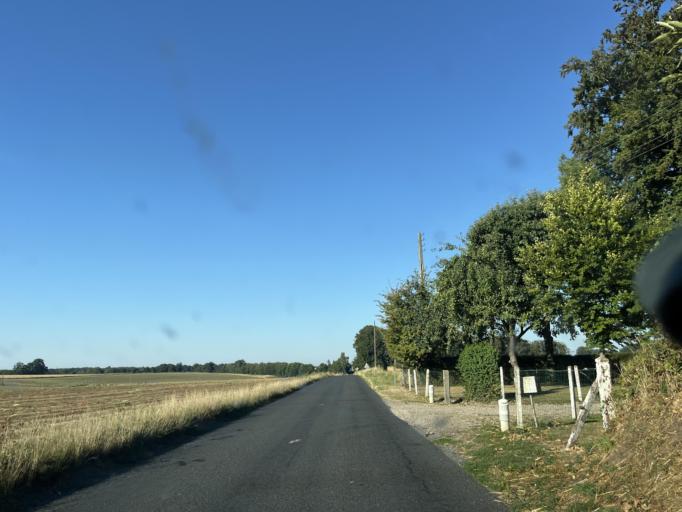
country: FR
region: Haute-Normandie
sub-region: Departement de la Seine-Maritime
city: Lillebonne
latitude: 49.5576
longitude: 0.5776
